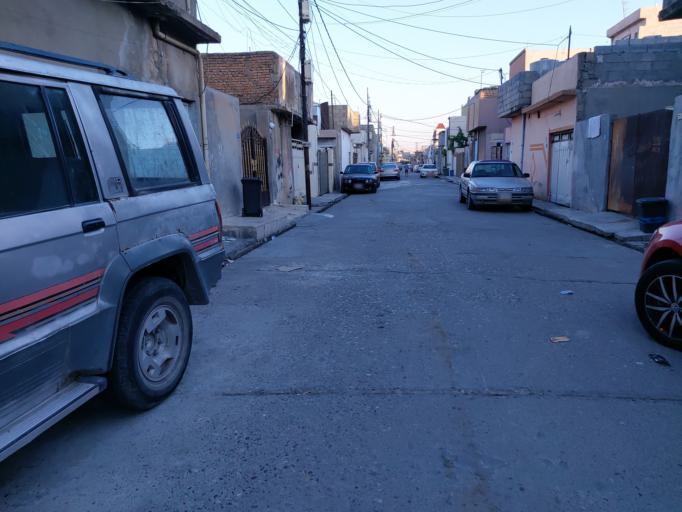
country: IQ
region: Arbil
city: Erbil
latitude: 36.1597
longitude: 43.9909
